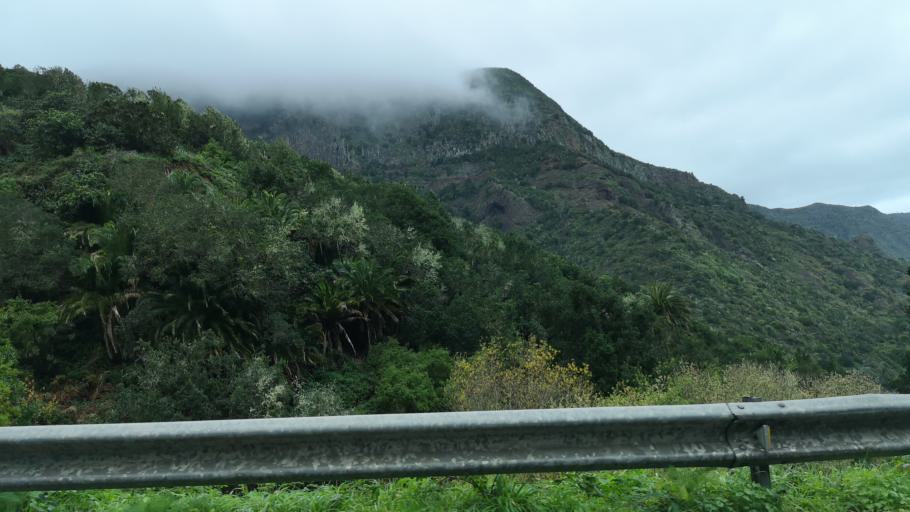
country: ES
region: Canary Islands
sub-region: Provincia de Santa Cruz de Tenerife
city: Hermigua
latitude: 28.1310
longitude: -17.1996
